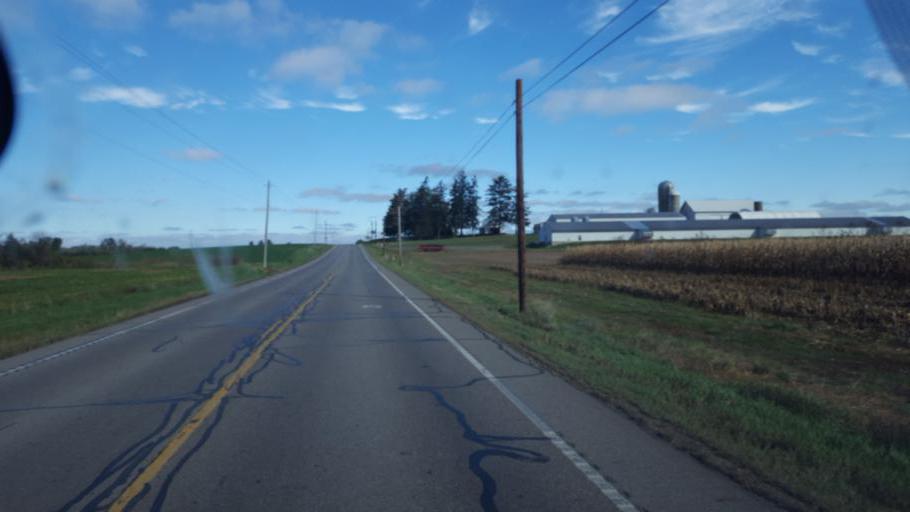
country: US
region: Ohio
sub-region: Huron County
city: Greenwich
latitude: 40.9489
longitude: -82.4949
